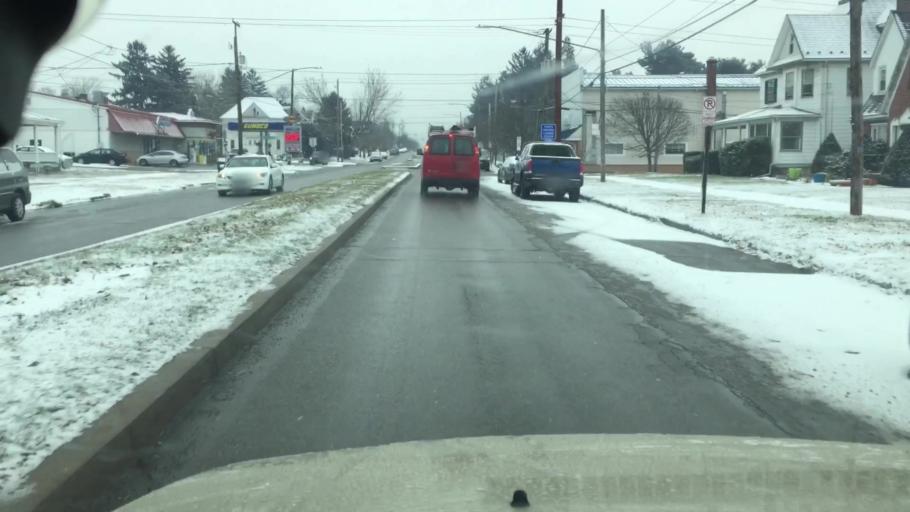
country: US
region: Pennsylvania
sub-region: Columbia County
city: Berwick
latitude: 41.0609
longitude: -76.2389
